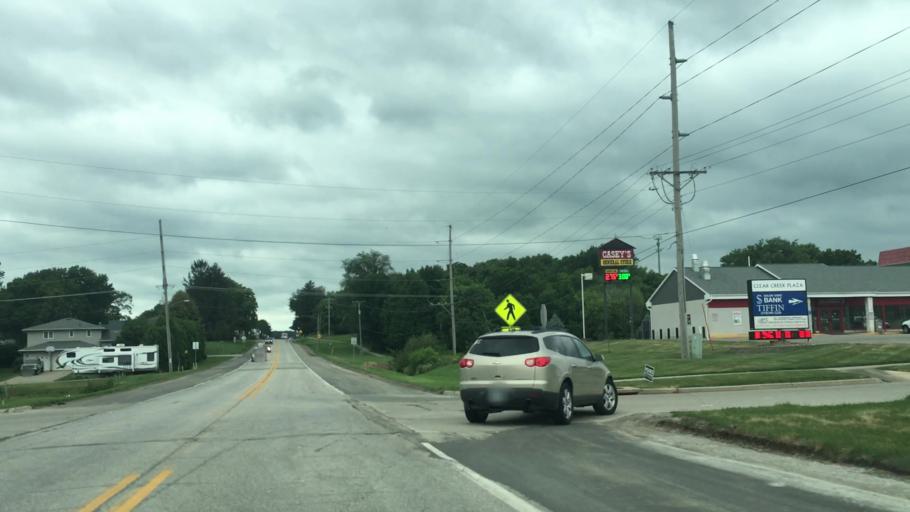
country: US
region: Iowa
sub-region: Johnson County
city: Tiffin
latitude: 41.7068
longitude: -91.6601
